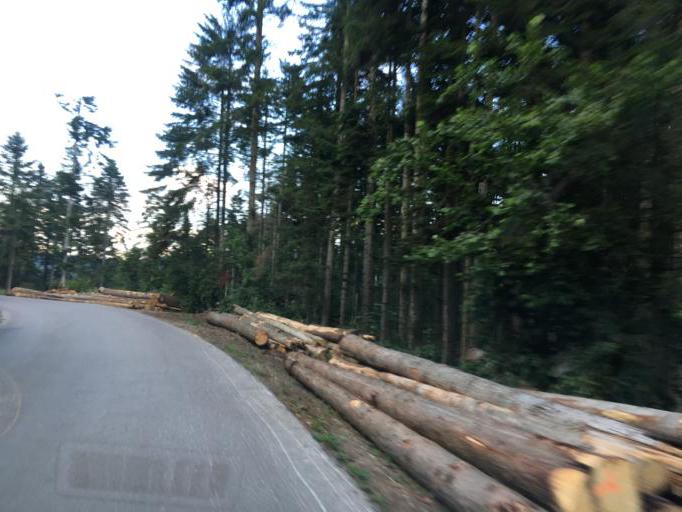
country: SI
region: Postojna
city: Postojna
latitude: 45.7967
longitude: 14.2004
